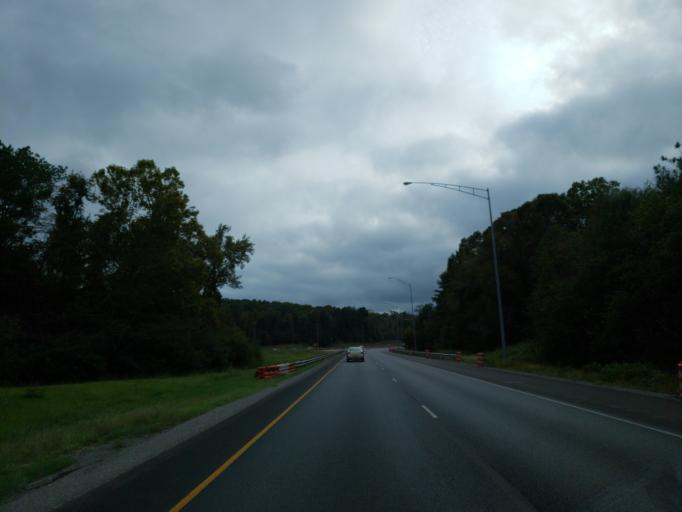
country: US
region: Alabama
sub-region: Jefferson County
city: Bessemer
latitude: 33.3382
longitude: -87.0343
